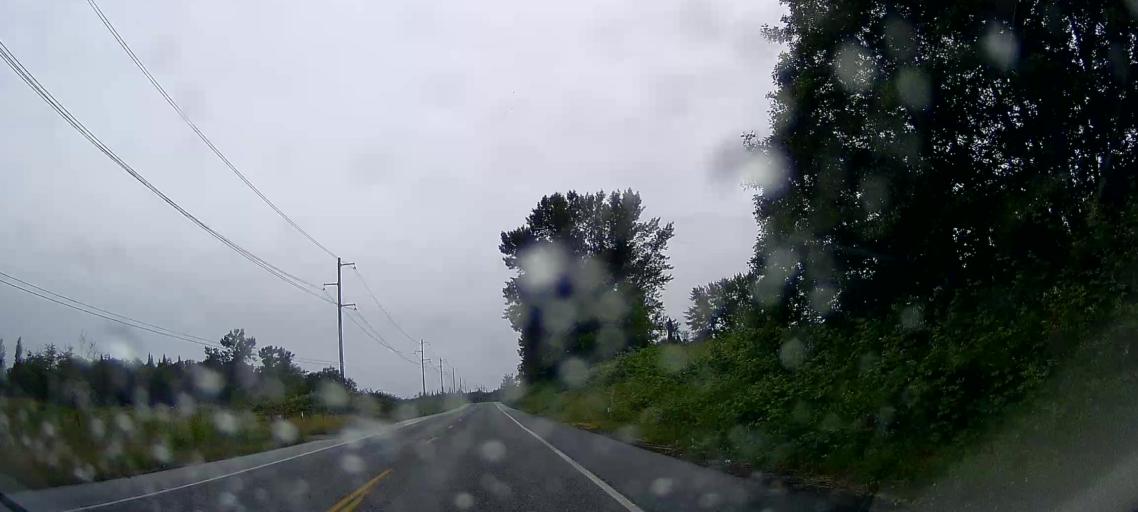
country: US
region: Washington
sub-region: Whatcom County
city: Birch Bay
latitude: 48.8500
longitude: -122.6961
